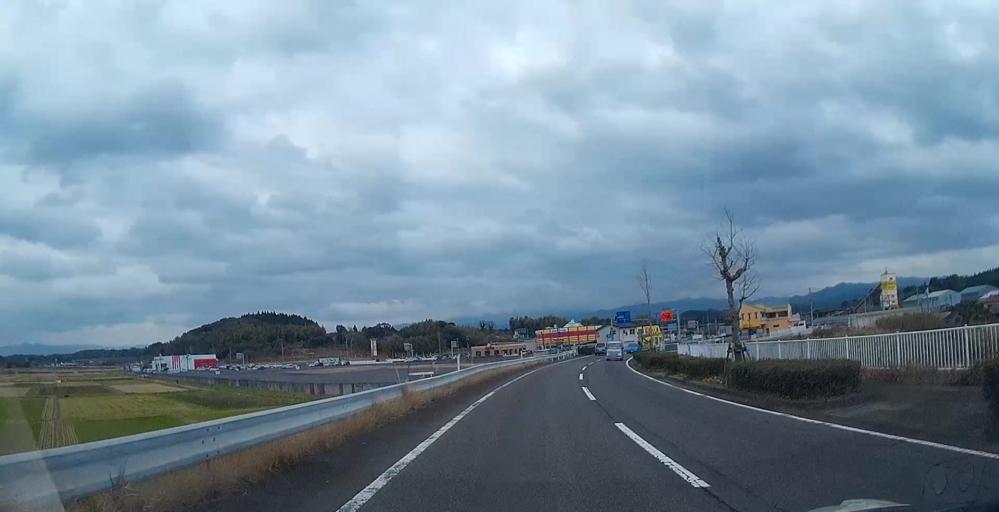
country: JP
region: Kagoshima
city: Akune
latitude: 32.0631
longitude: 130.2252
